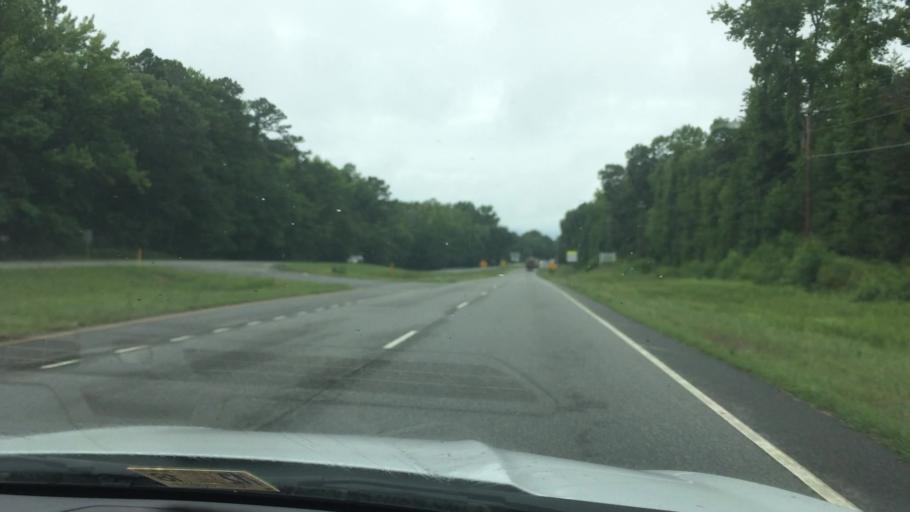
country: US
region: Virginia
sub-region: King William County
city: West Point
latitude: 37.5382
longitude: -76.7621
